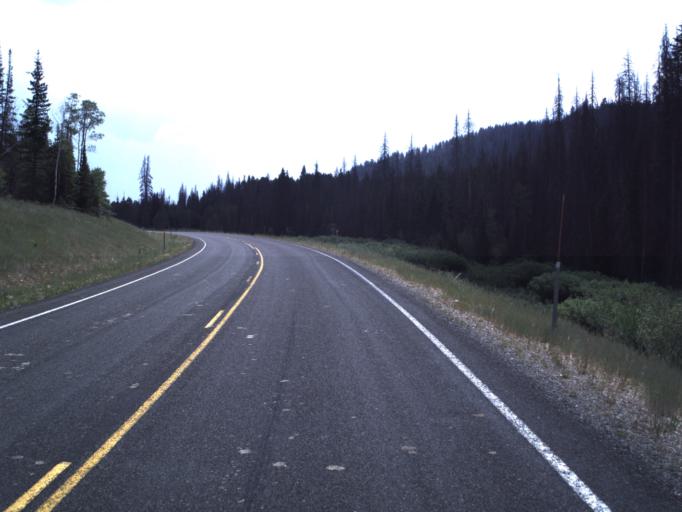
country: US
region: Utah
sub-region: Summit County
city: Francis
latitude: 40.4916
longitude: -110.9686
